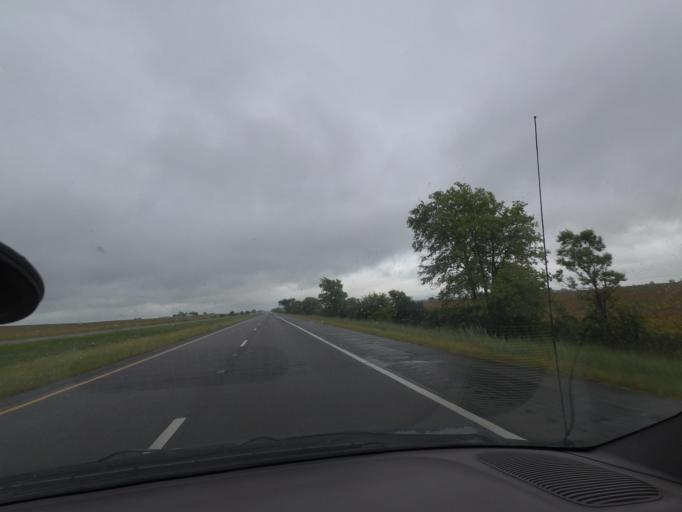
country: US
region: Illinois
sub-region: Champaign County
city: Mahomet
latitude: 40.1203
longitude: -88.4585
